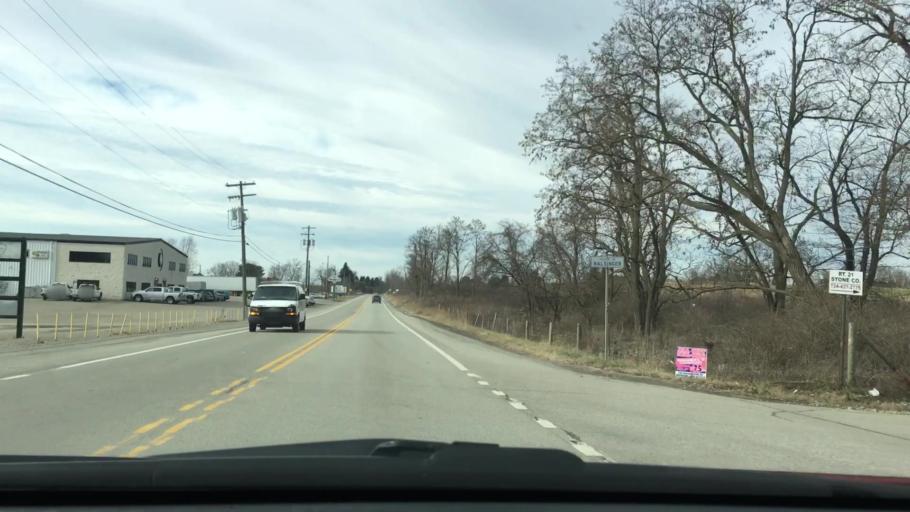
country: US
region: Pennsylvania
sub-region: Fayette County
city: South Uniontown
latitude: 39.8933
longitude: -79.8009
